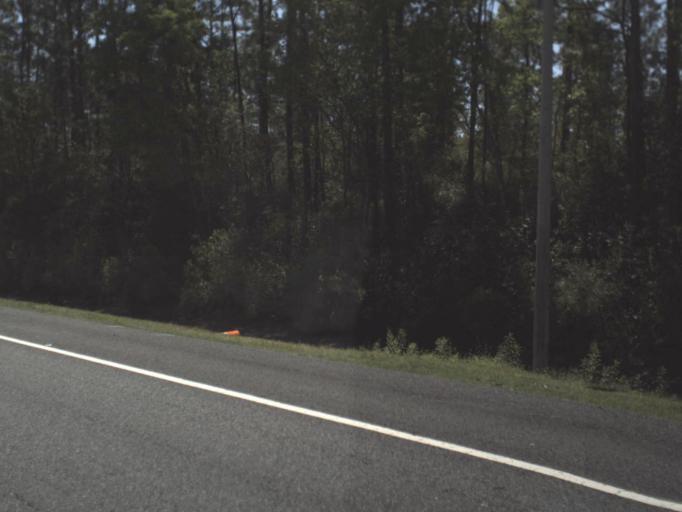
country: US
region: Florida
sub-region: Escambia County
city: Cantonment
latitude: 30.5673
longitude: -87.3923
